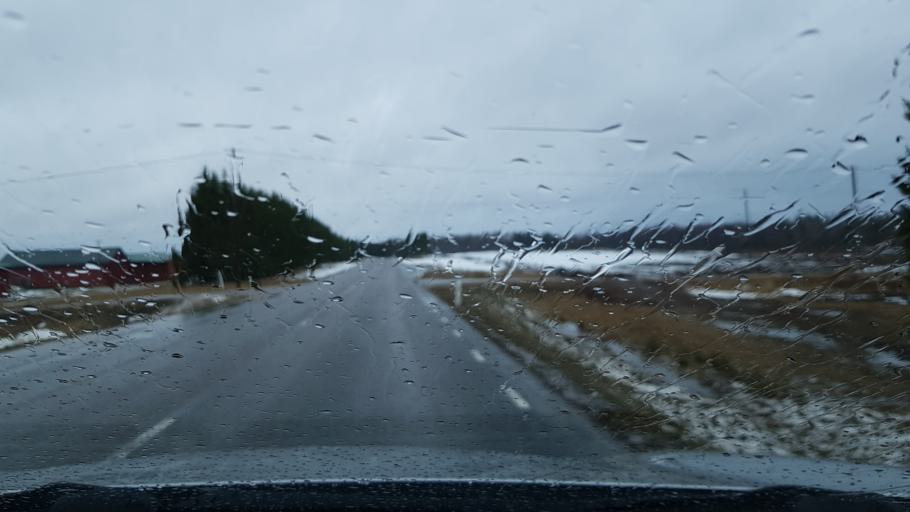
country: LV
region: Apes Novads
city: Ape
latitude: 57.5882
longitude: 26.6429
